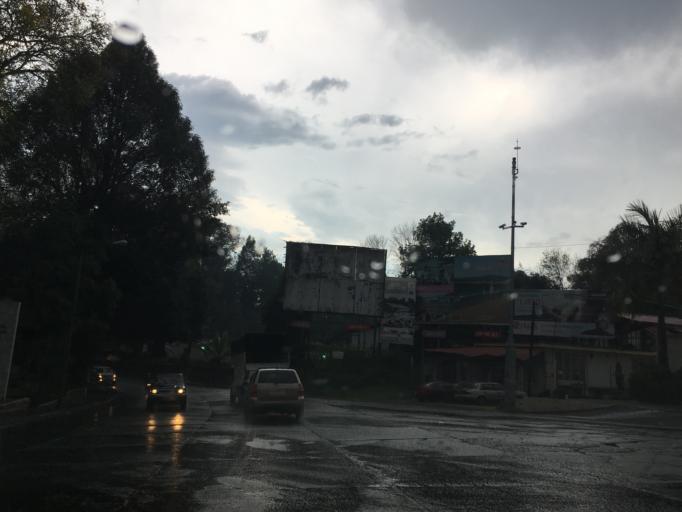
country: MX
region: Michoacan
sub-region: Uruapan
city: Uruapan
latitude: 19.4293
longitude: -102.0729
